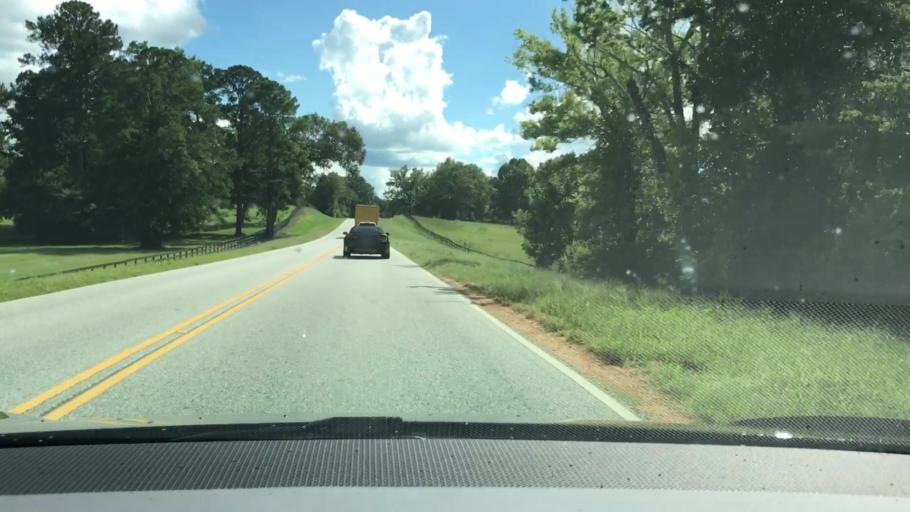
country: US
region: Alabama
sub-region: Montgomery County
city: Pike Road
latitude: 32.2146
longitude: -86.0908
